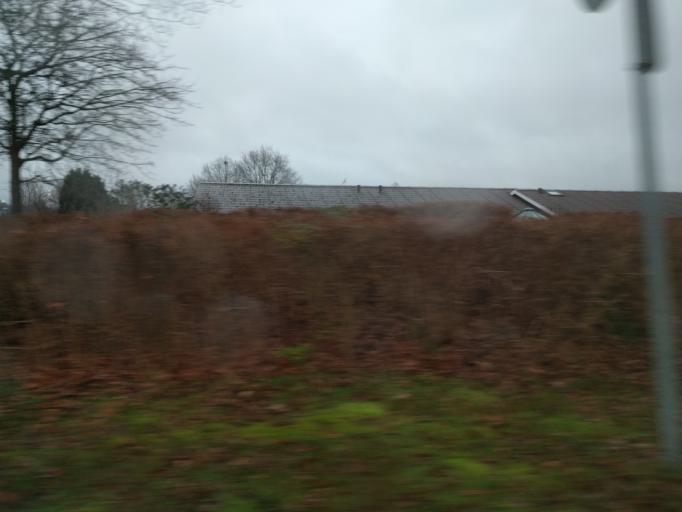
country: DK
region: South Denmark
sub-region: Odense Kommune
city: Neder Holluf
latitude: 55.3743
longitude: 10.4505
